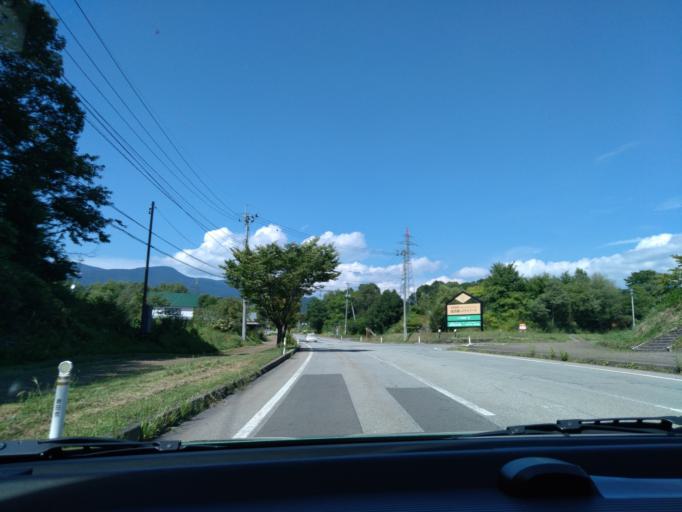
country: JP
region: Akita
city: Kakunodatemachi
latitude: 39.7418
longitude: 140.7192
